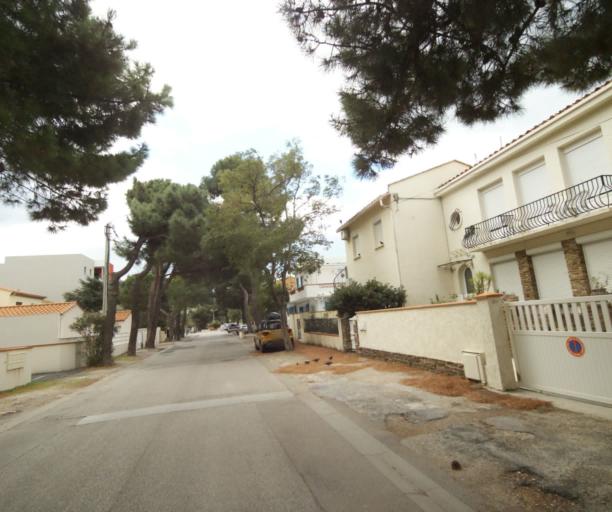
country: FR
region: Languedoc-Roussillon
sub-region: Departement des Pyrenees-Orientales
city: Argelers
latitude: 42.5603
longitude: 3.0455
